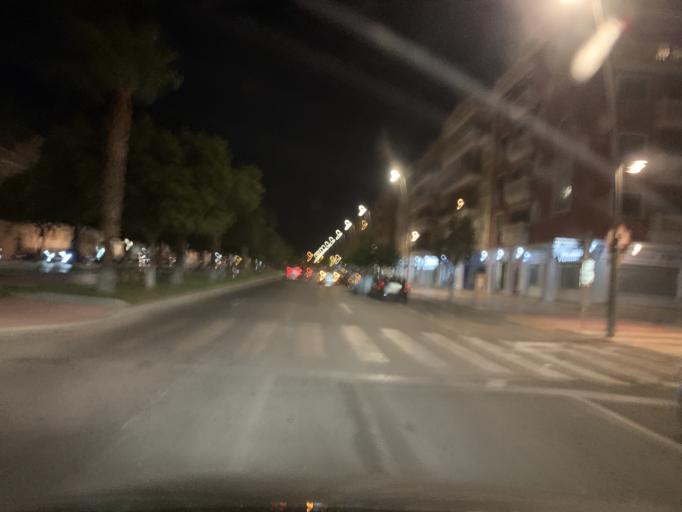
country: ES
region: Andalusia
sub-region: Provincia de Almeria
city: Roquetas de Mar
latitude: 36.7751
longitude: -2.6088
